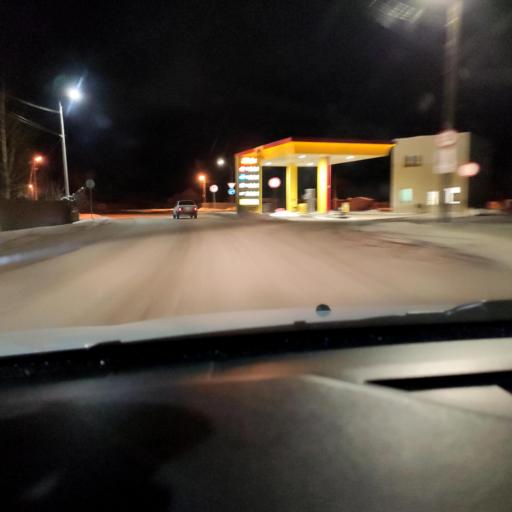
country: RU
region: Samara
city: Smyshlyayevka
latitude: 53.2512
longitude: 50.3832
